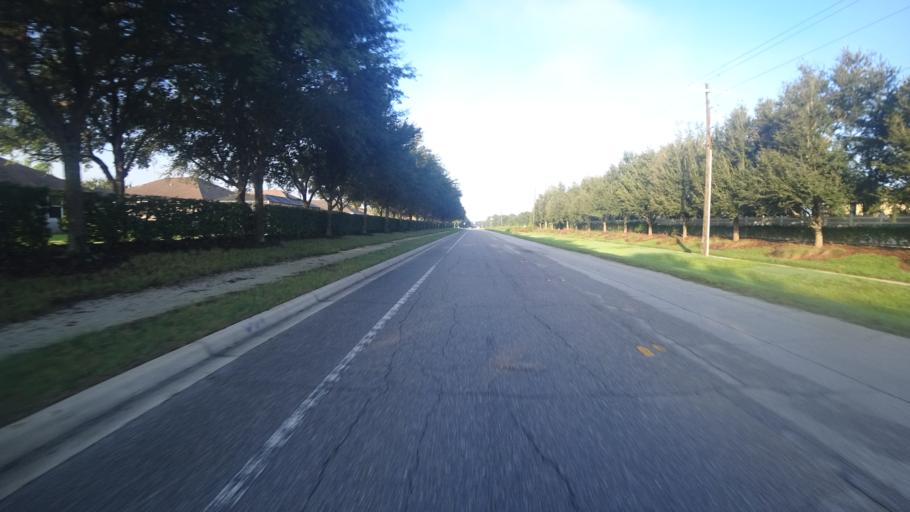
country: US
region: Florida
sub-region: Manatee County
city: Ellenton
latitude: 27.5353
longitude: -82.4186
